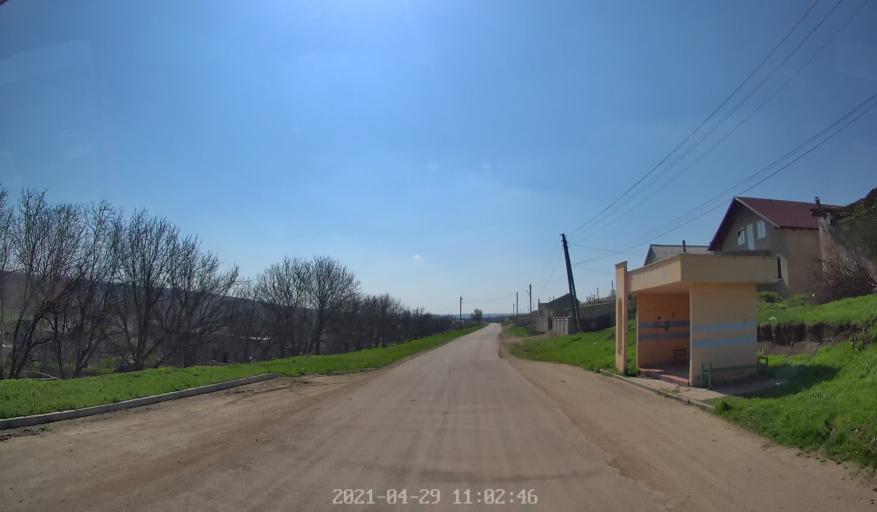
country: MD
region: Chisinau
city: Ciorescu
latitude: 47.1612
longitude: 28.9532
